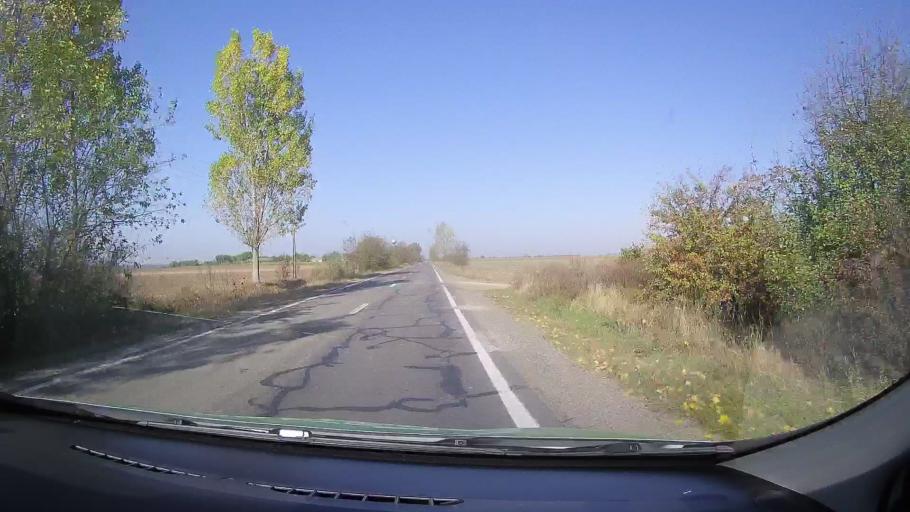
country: RO
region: Satu Mare
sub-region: Comuna Urziceni
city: Urziceni
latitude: 47.7181
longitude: 22.4191
